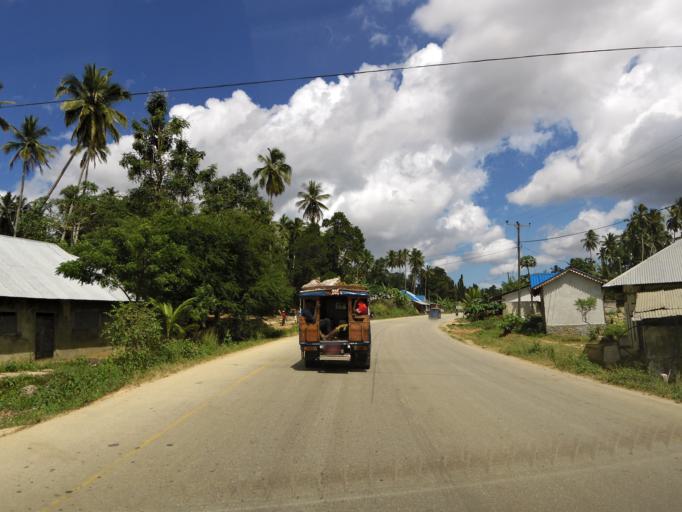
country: TZ
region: Zanzibar Central/South
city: Koani
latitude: -6.1401
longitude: 39.2841
